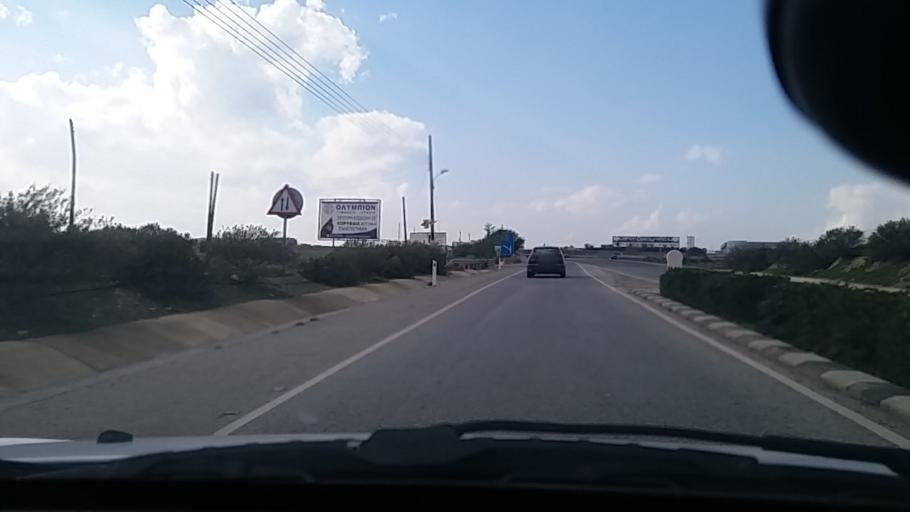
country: CY
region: Lefkosia
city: Kokkinotrimithia
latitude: 35.1496
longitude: 33.2375
